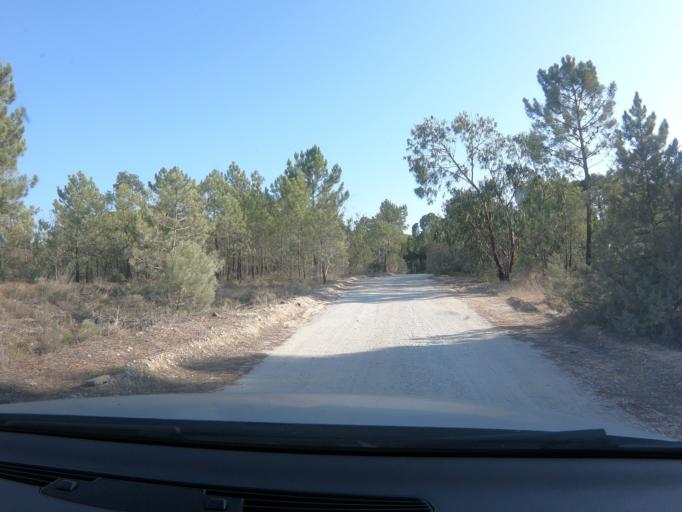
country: PT
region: Setubal
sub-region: Setubal
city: Setubal
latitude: 38.4777
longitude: -8.8801
